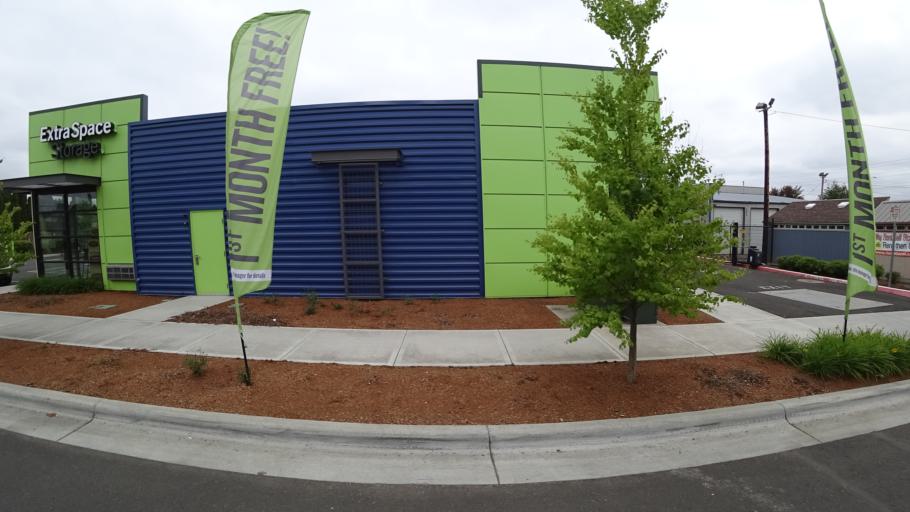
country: US
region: Oregon
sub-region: Washington County
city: Aloha
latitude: 45.4987
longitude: -122.9073
